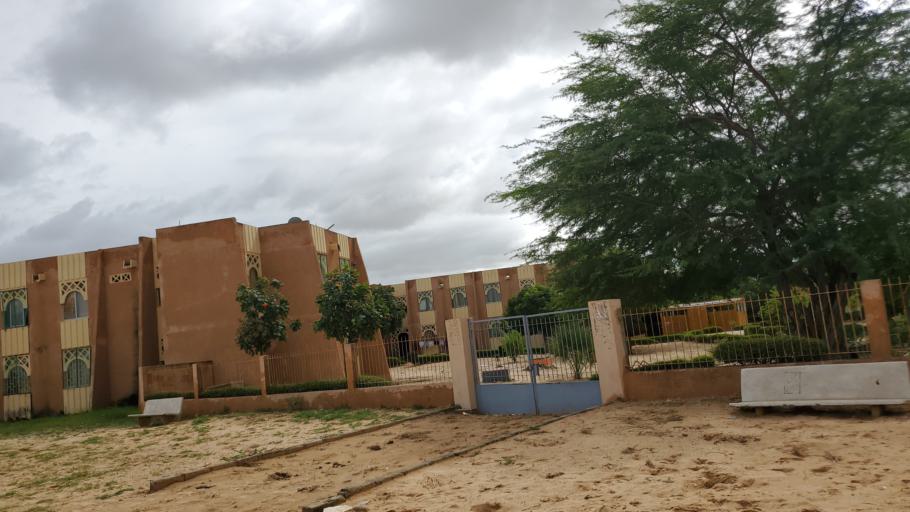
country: SN
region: Saint-Louis
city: Saint-Louis
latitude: 16.0627
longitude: -16.4272
